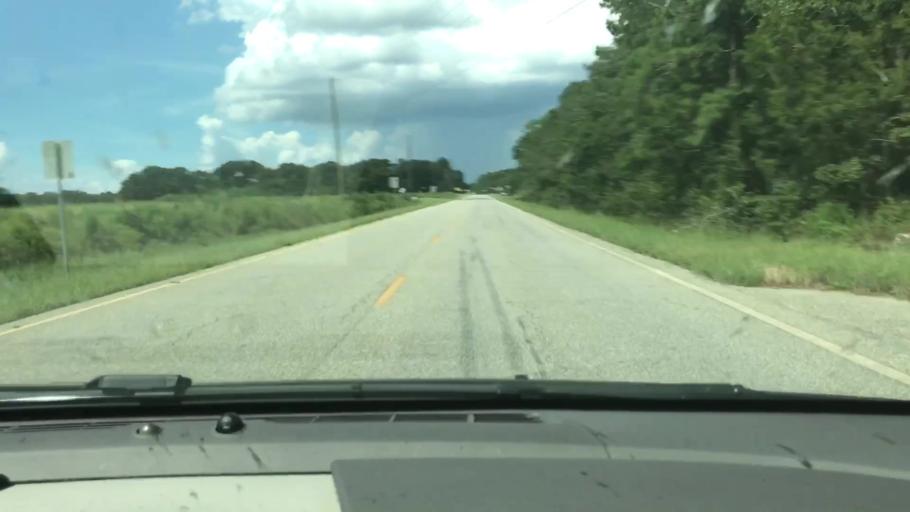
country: US
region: Georgia
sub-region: Quitman County
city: Georgetown
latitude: 31.7777
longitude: -85.0918
